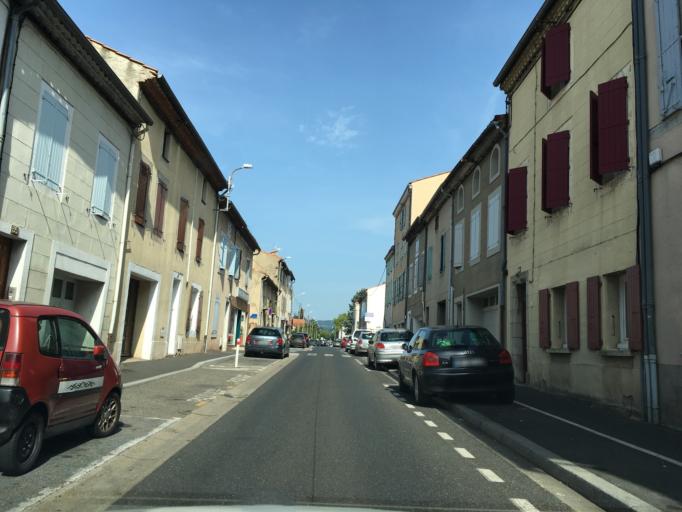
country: FR
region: Midi-Pyrenees
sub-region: Departement du Tarn
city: Castres
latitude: 43.6062
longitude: 2.2476
